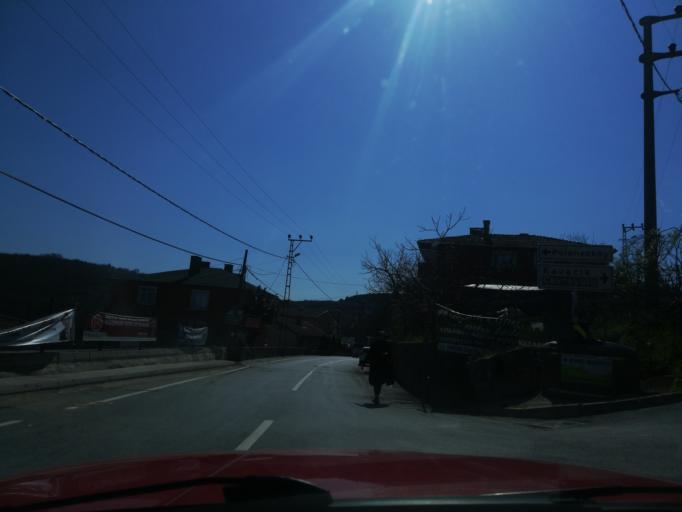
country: TR
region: Istanbul
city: Mahmut Sevket Pasa
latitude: 41.1272
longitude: 29.1589
